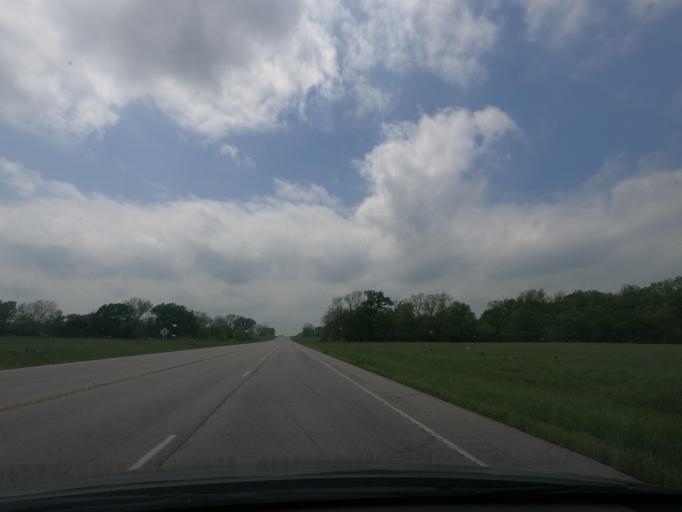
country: US
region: Kansas
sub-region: Labette County
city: Parsons
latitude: 37.3402
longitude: -95.1434
